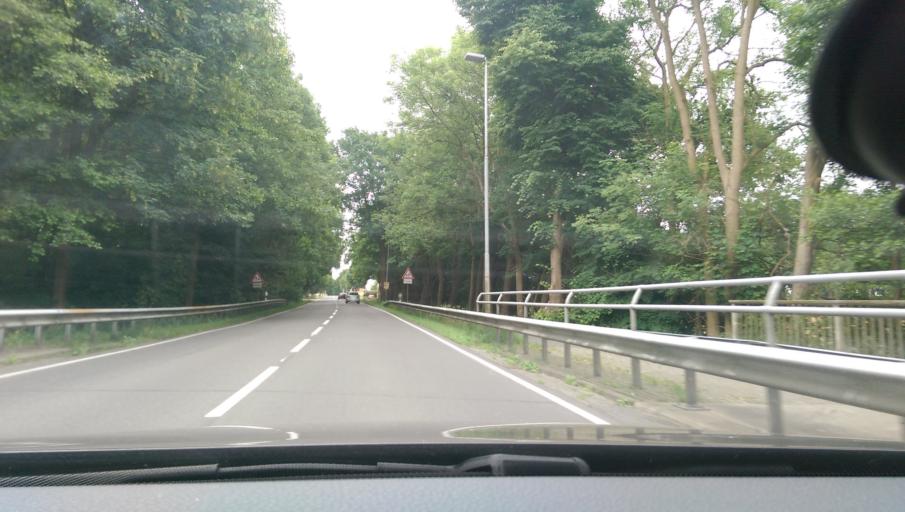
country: DE
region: Lower Saxony
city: Gyhum
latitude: 53.1763
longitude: 9.2913
